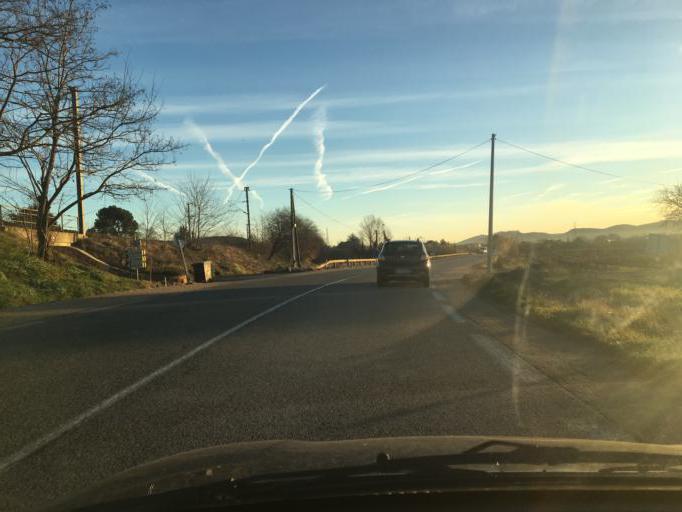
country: FR
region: Provence-Alpes-Cote d'Azur
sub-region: Departement du Var
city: Taradeau
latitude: 43.4501
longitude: 6.4525
